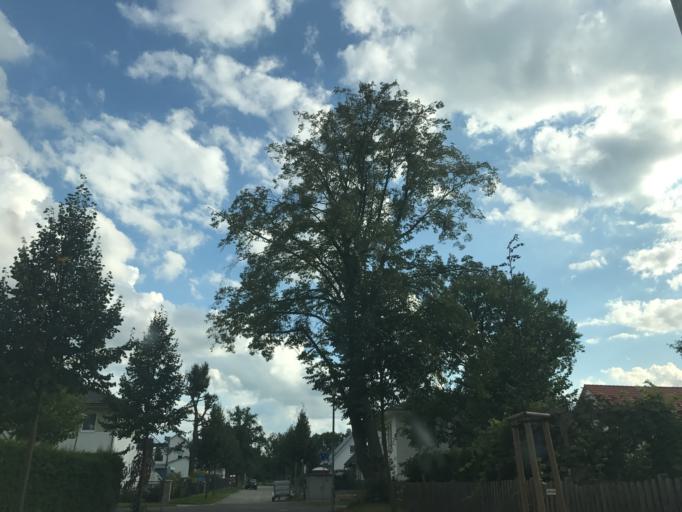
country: DE
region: Brandenburg
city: Dallgow-Doeberitz
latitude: 52.5373
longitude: 13.0517
